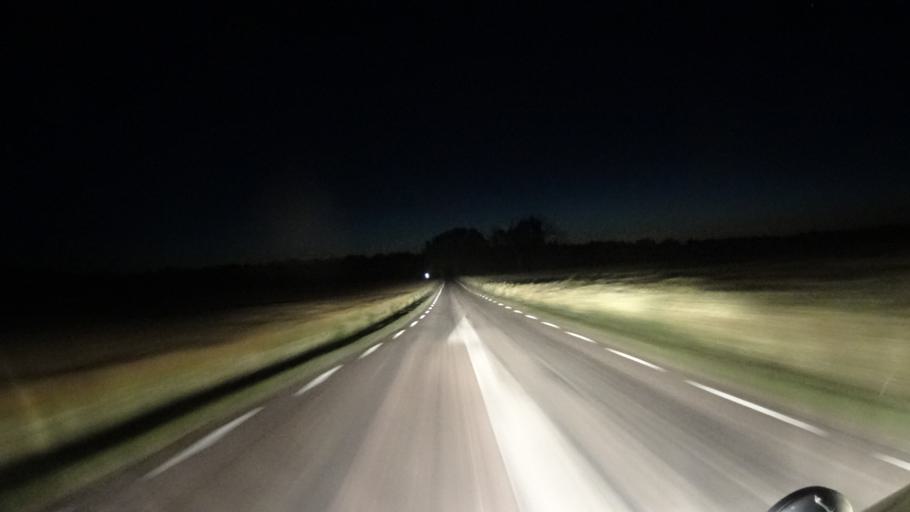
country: SE
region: OEstergoetland
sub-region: Vadstena Kommun
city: Herrestad
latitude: 58.3146
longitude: 14.8432
